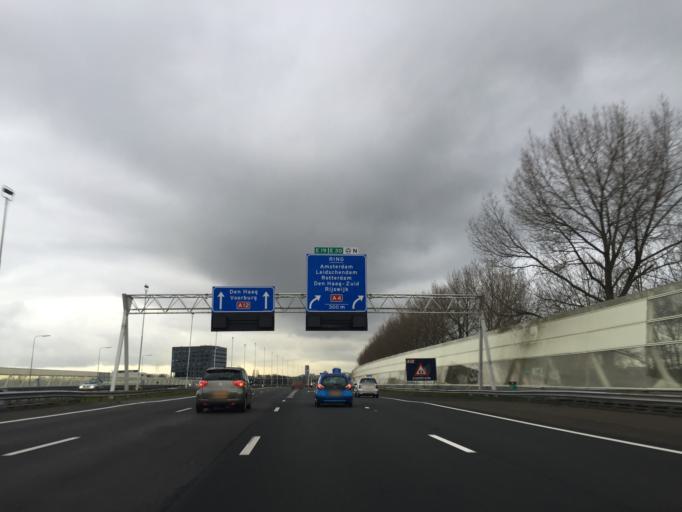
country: NL
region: South Holland
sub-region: Gemeente Den Haag
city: Ypenburg
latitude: 52.0552
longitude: 4.3961
